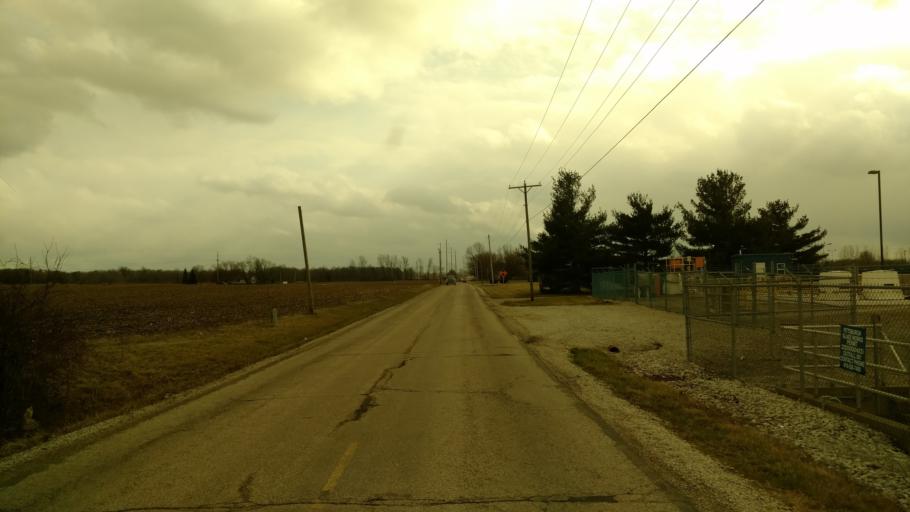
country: US
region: Ohio
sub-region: Crawford County
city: Crestline
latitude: 40.7895
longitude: -82.6977
